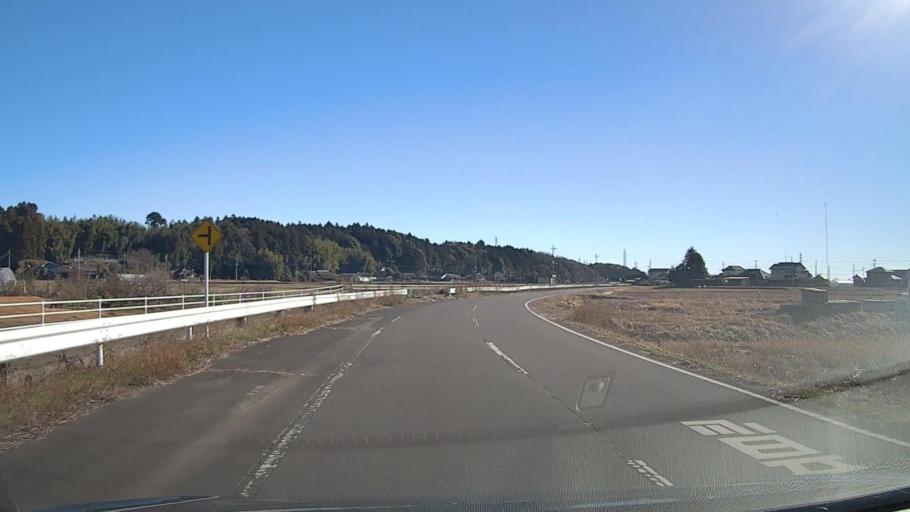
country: JP
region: Ibaraki
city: Mito-shi
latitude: 36.4410
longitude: 140.4349
